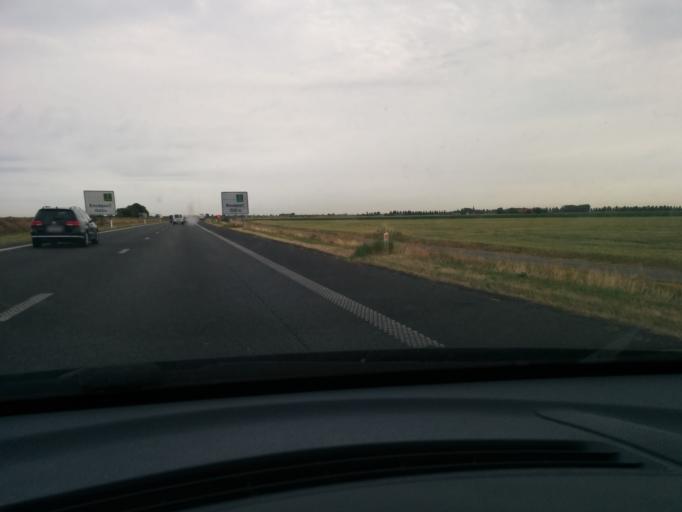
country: BE
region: Flanders
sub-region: Provincie West-Vlaanderen
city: Nieuwpoort
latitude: 51.0973
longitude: 2.7363
